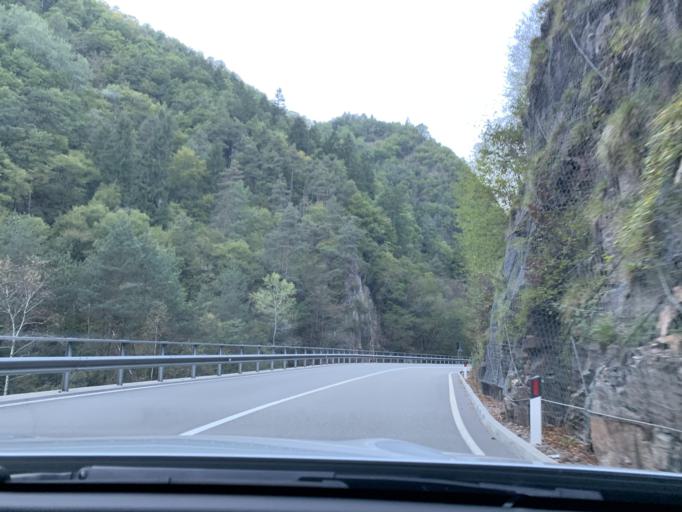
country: IT
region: Trentino-Alto Adige
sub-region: Bolzano
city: Cornedo All'Isarco
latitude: 46.4665
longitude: 11.4093
